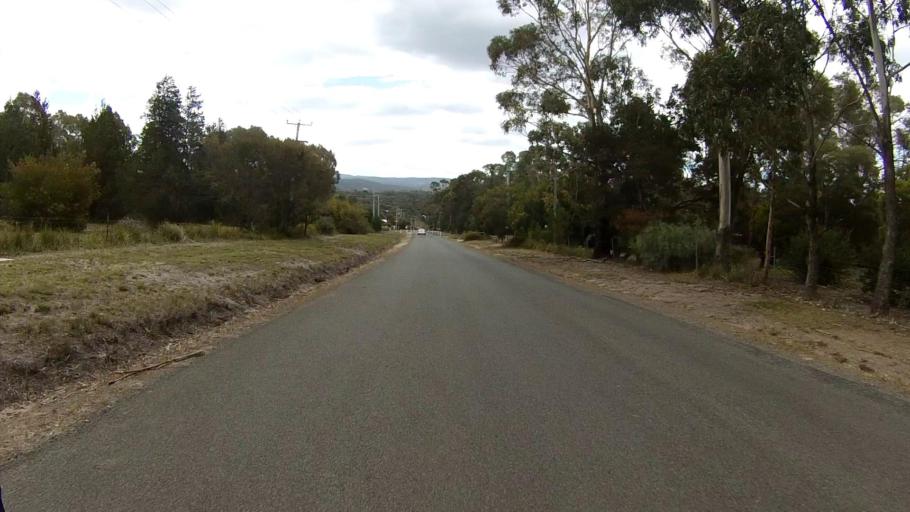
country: AU
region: Tasmania
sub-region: Sorell
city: Sorell
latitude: -42.5860
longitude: 147.9142
